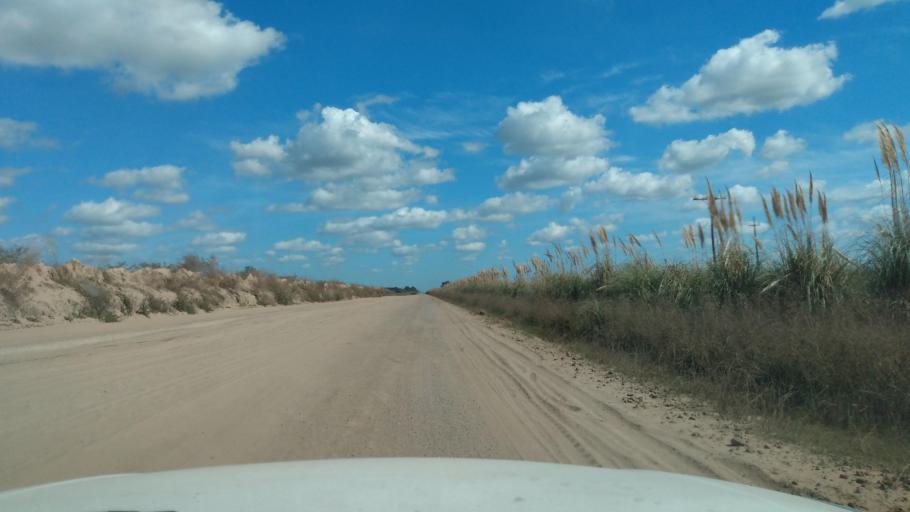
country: AR
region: Buenos Aires
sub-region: Partido de Navarro
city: Navarro
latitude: -35.0031
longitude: -59.3628
